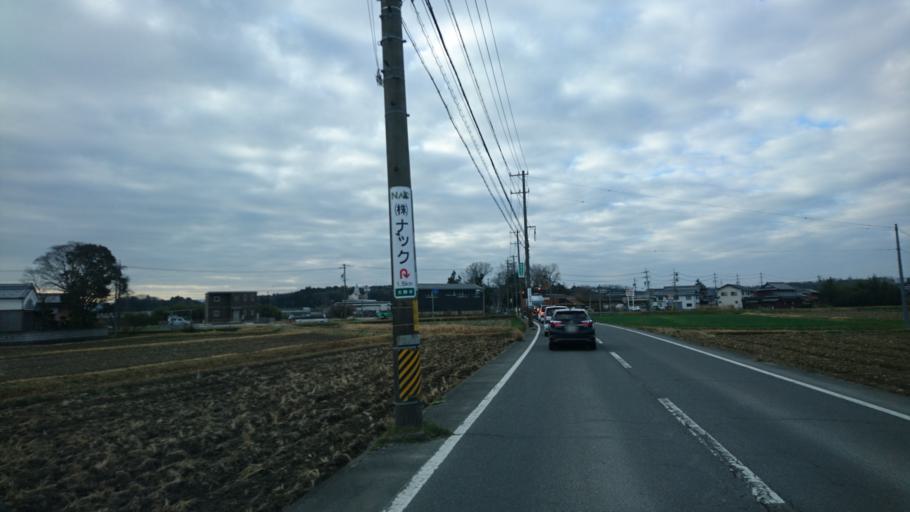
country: JP
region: Mie
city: Ueno-ebisumachi
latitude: 34.7437
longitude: 136.1096
